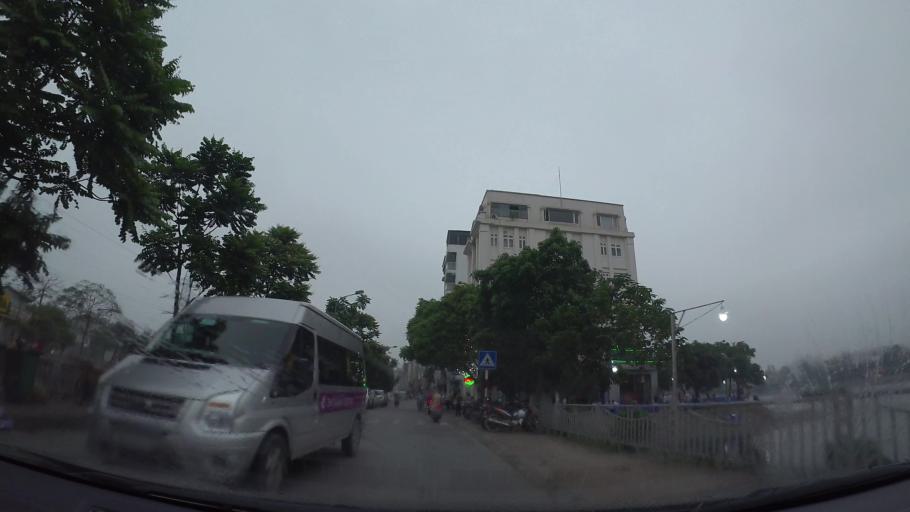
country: VN
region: Ha Noi
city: Hai BaTrung
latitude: 20.9947
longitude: 105.8364
